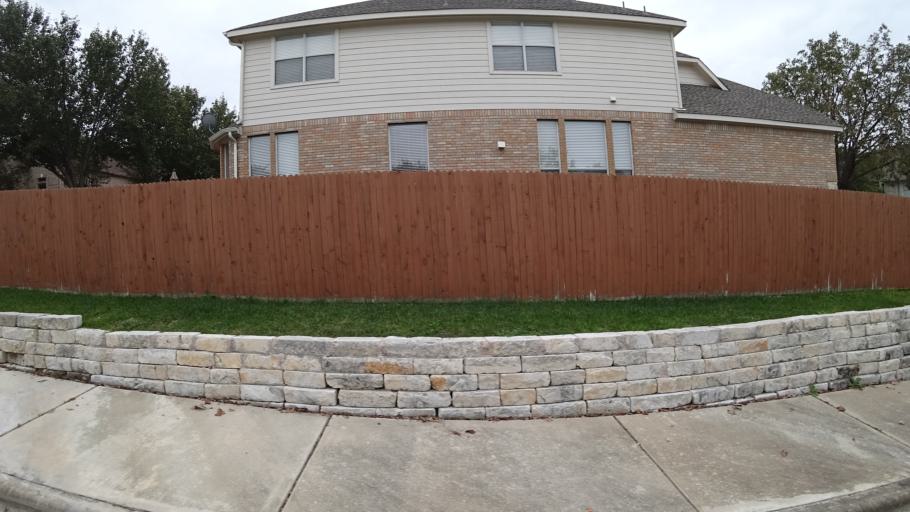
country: US
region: Texas
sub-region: Travis County
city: Bee Cave
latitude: 30.3130
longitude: -97.9236
